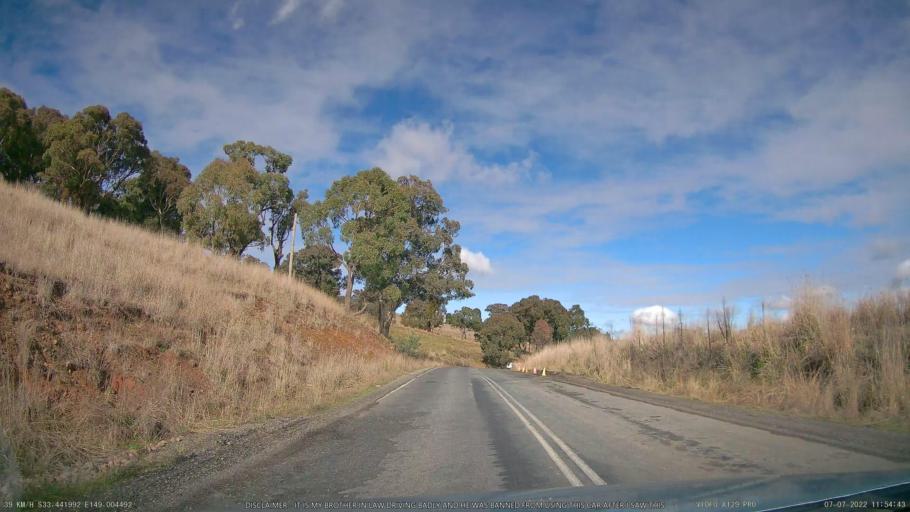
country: AU
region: New South Wales
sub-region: Blayney
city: Millthorpe
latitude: -33.4422
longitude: 149.0044
